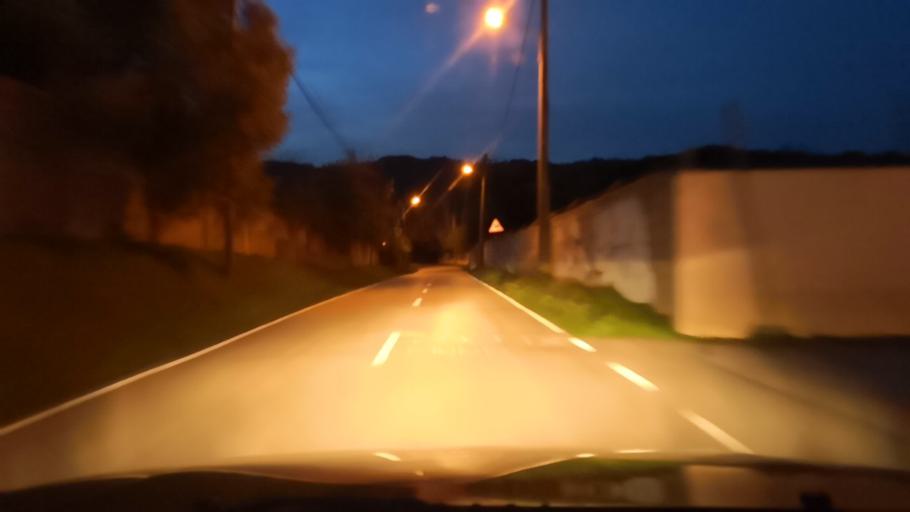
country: PT
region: Setubal
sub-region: Setubal
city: Setubal
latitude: 38.5380
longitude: -8.9023
